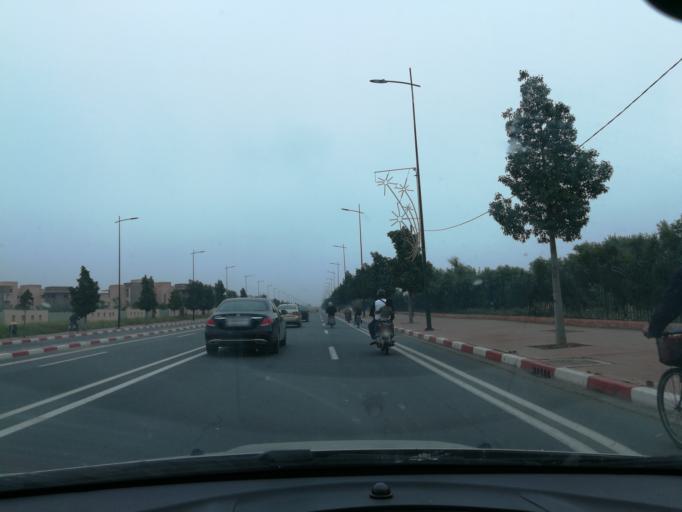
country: MA
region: Marrakech-Tensift-Al Haouz
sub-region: Marrakech
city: Marrakesh
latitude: 31.6095
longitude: -8.0043
